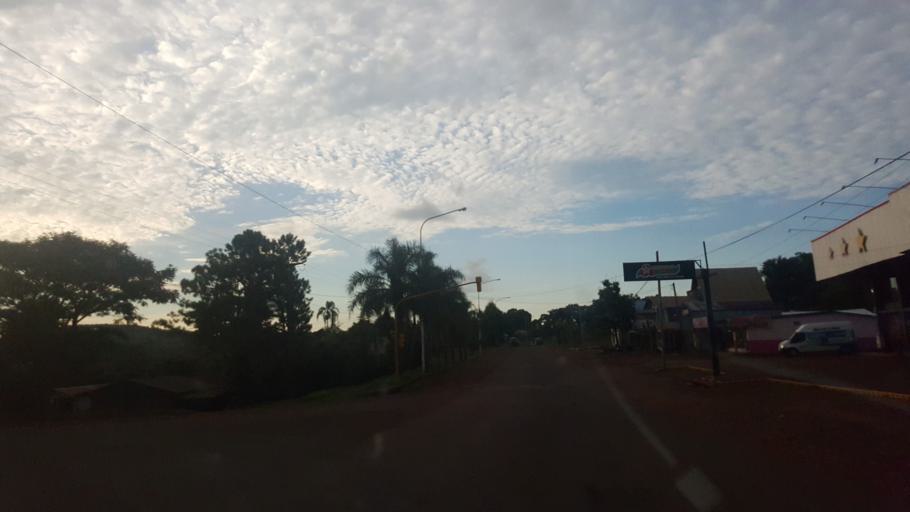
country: AR
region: Misiones
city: Dos de Mayo
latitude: -27.0364
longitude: -54.6850
